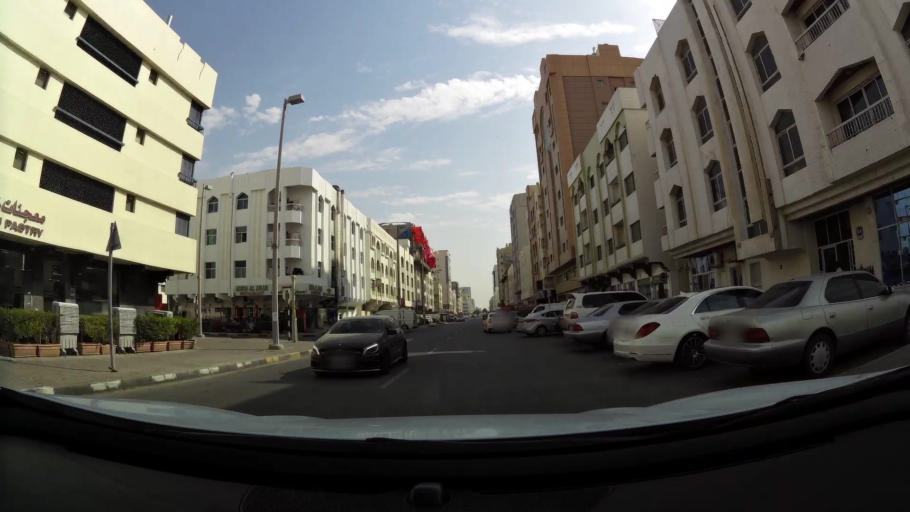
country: AE
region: Abu Dhabi
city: Abu Dhabi
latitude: 24.3288
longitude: 54.5370
